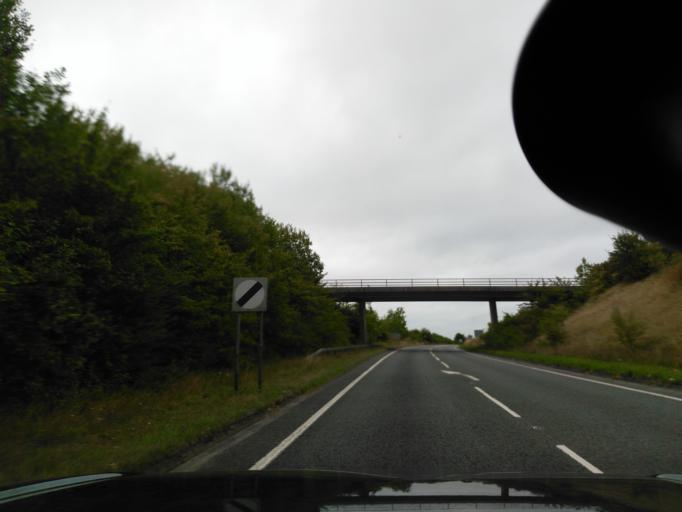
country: GB
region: England
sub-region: Wiltshire
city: Upton Scudamore
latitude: 51.2305
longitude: -2.1878
